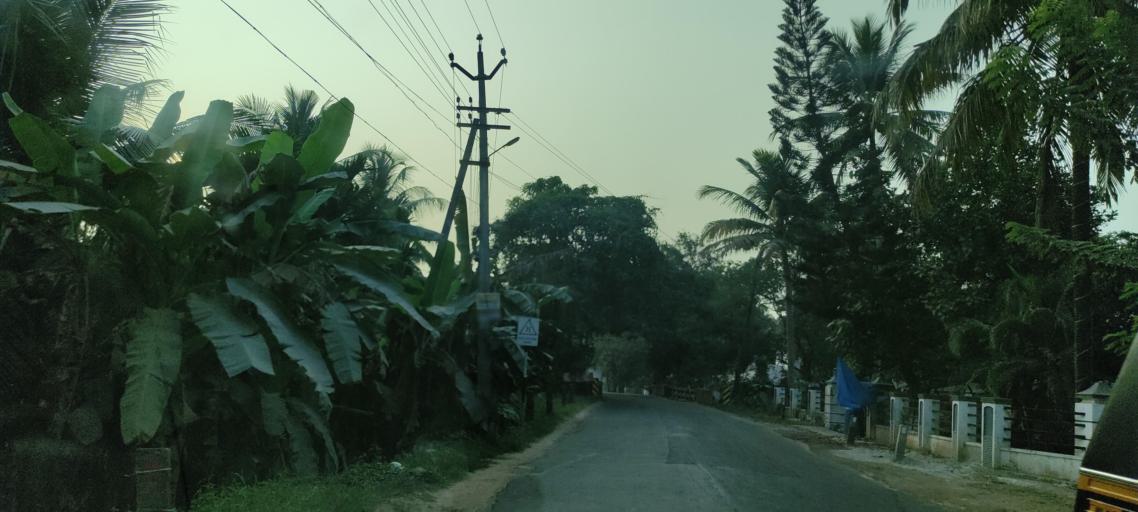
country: IN
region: Kerala
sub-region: Kottayam
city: Vaikam
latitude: 9.6878
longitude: 76.4276
